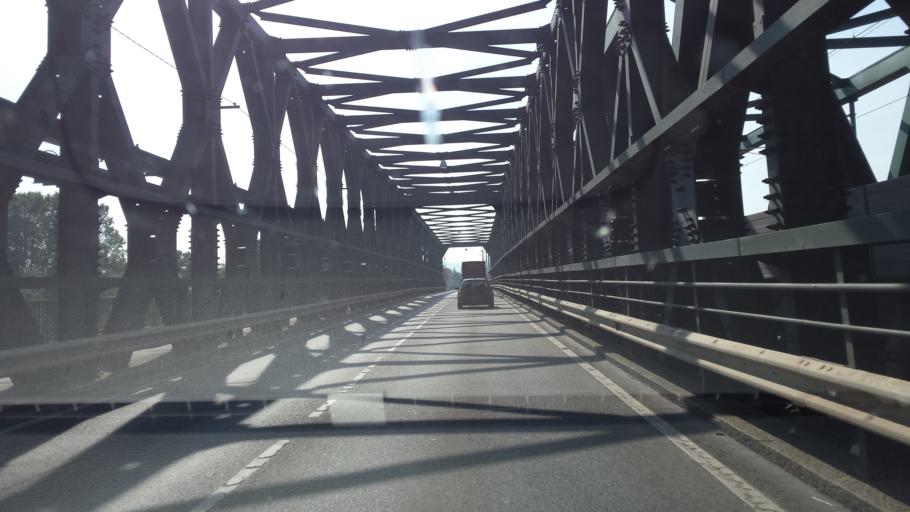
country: AT
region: Lower Austria
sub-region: Politischer Bezirk Tulln
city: Tulln
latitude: 48.3351
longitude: 16.0590
